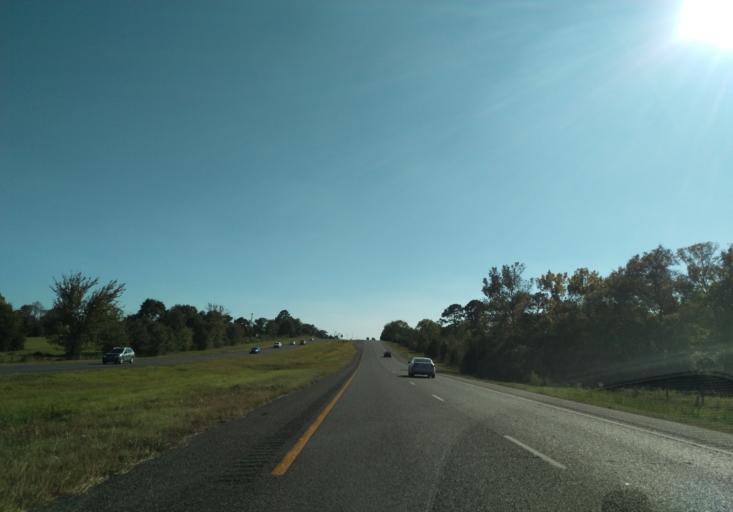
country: US
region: Texas
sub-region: Waller County
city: Hempstead
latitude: 30.2010
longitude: -96.0599
